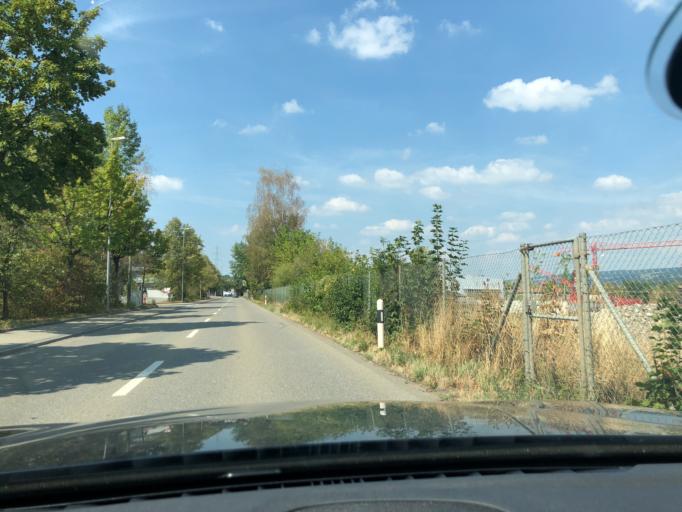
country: CH
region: Aargau
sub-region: Bezirk Bremgarten
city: Bremgarten
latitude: 47.3494
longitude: 8.3310
